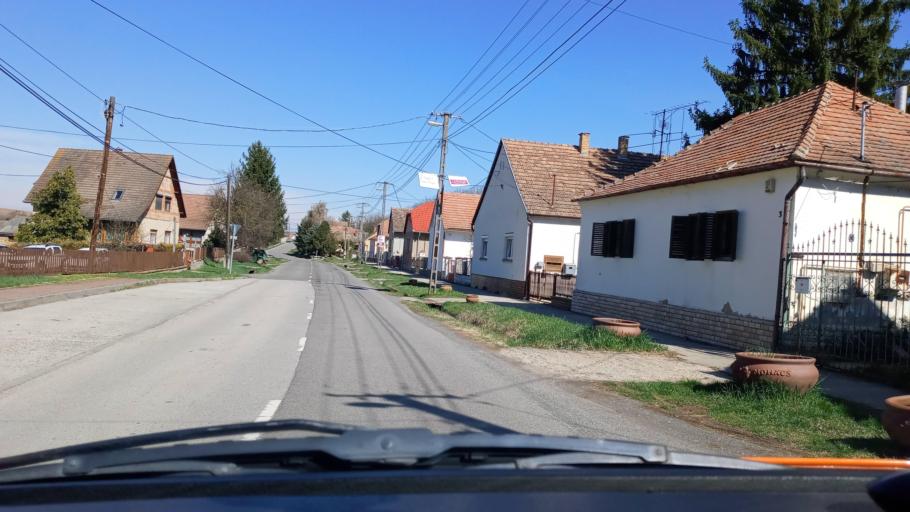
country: HU
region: Baranya
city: Boly
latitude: 45.9972
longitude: 18.4603
